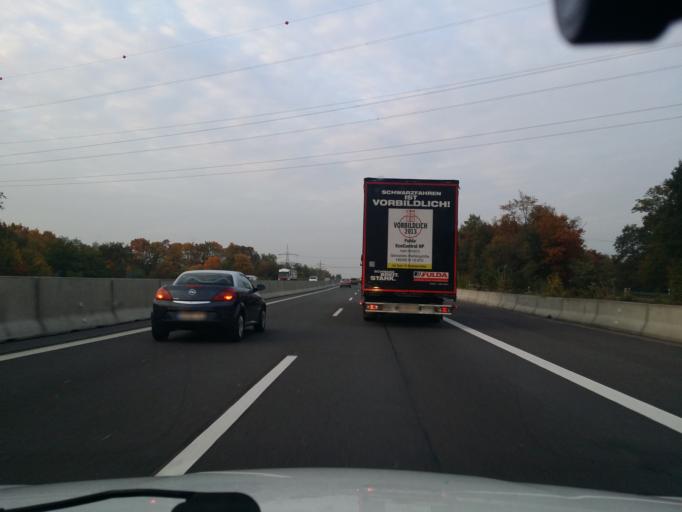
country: DE
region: Hesse
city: Viernheim
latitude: 49.5194
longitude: 8.5601
